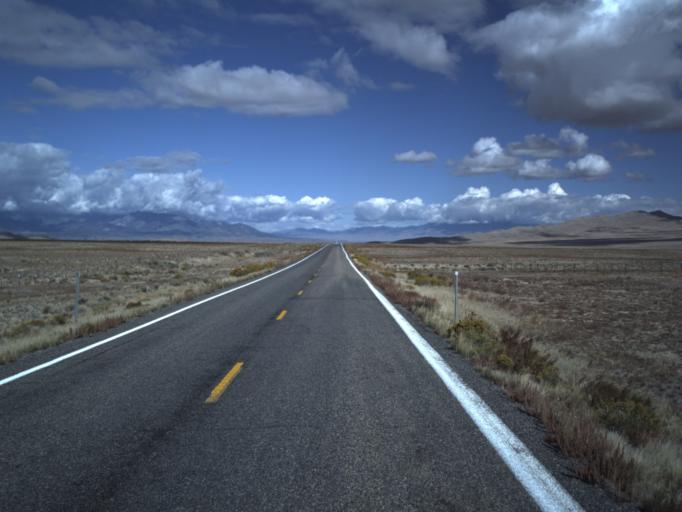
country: US
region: Utah
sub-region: Beaver County
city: Milford
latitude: 38.6637
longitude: -113.8793
